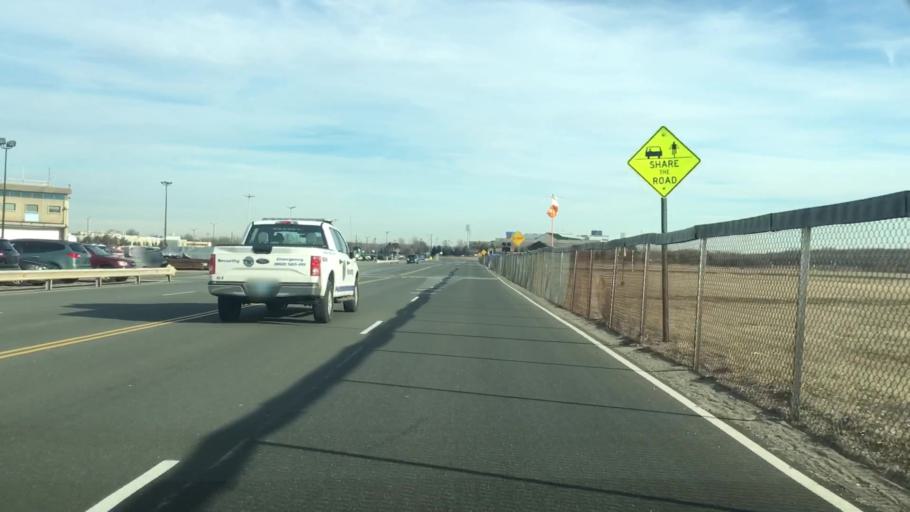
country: US
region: Connecticut
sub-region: Hartford County
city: East Hartford
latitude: 41.7510
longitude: -72.6266
